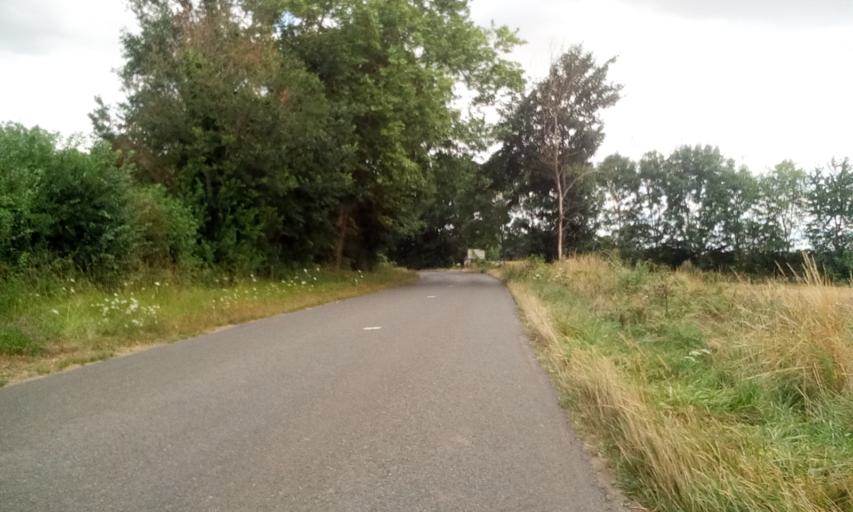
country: FR
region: Lower Normandy
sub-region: Departement du Calvados
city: Bellengreville
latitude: 49.1394
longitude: -0.2058
